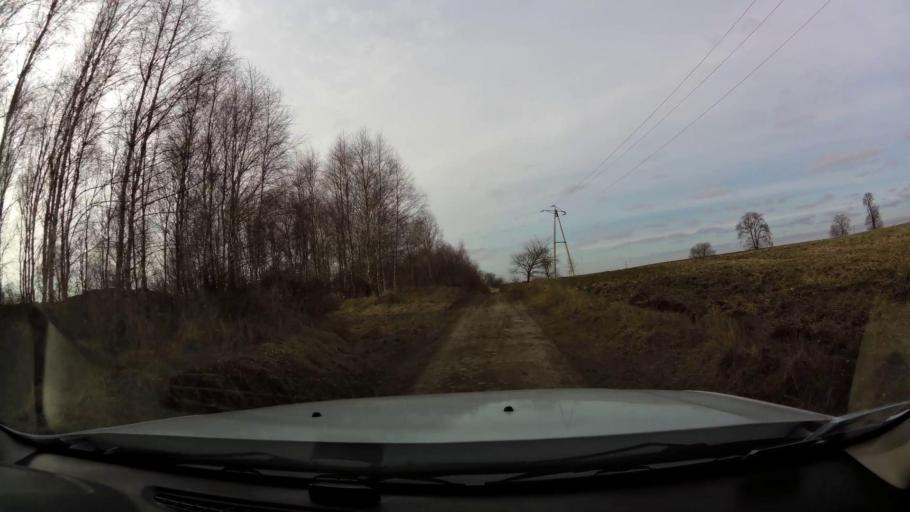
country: PL
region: West Pomeranian Voivodeship
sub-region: Powiat drawski
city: Drawsko Pomorskie
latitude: 53.5203
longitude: 15.7730
